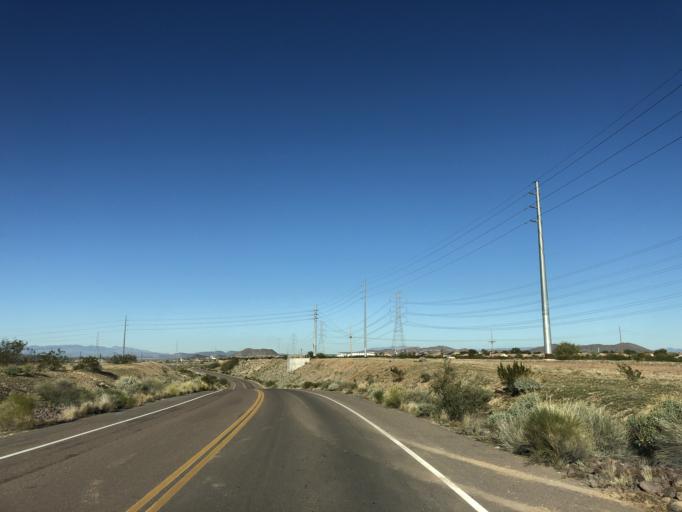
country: US
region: Arizona
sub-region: Maricopa County
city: Sun City West
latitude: 33.6796
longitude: -112.2989
